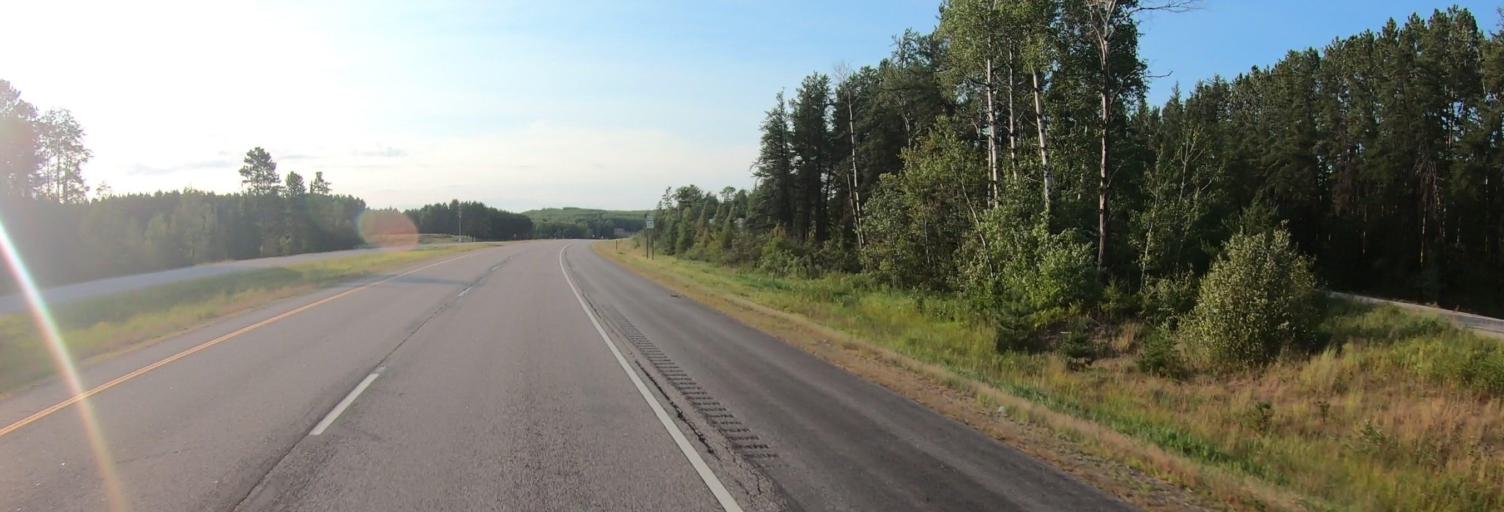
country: US
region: Minnesota
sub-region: Saint Louis County
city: Mountain Iron
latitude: 47.6739
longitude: -92.6331
